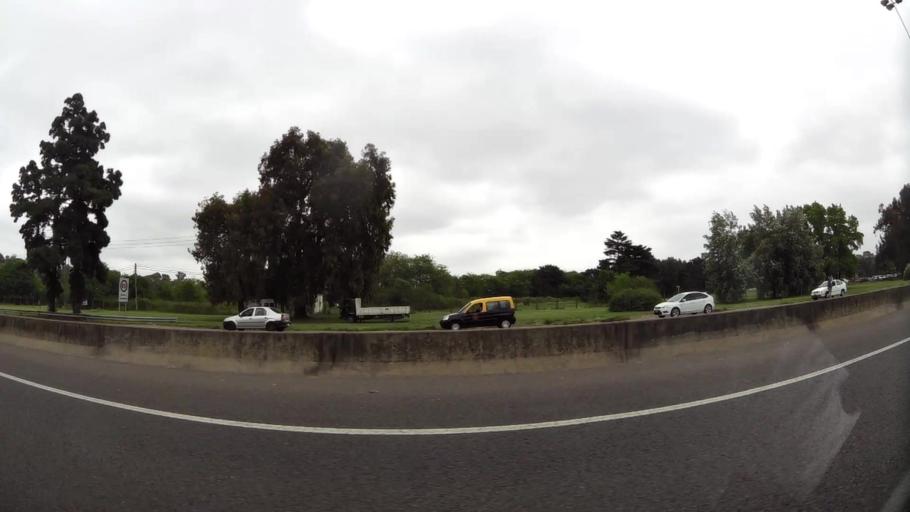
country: AR
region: Buenos Aires
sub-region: Partido de Ezeiza
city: Ezeiza
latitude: -34.7907
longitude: -58.5270
